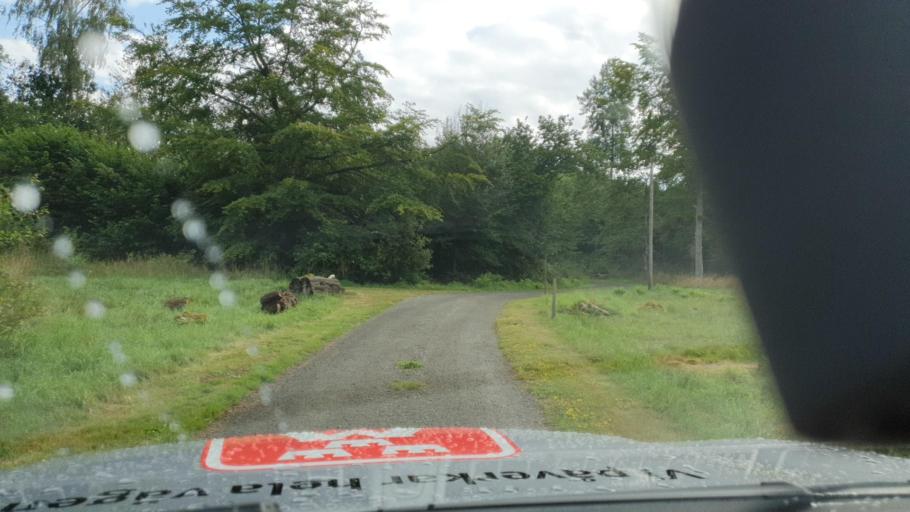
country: SE
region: Skane
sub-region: Hassleholms Kommun
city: Vinslov
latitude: 56.0450
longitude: 13.8683
